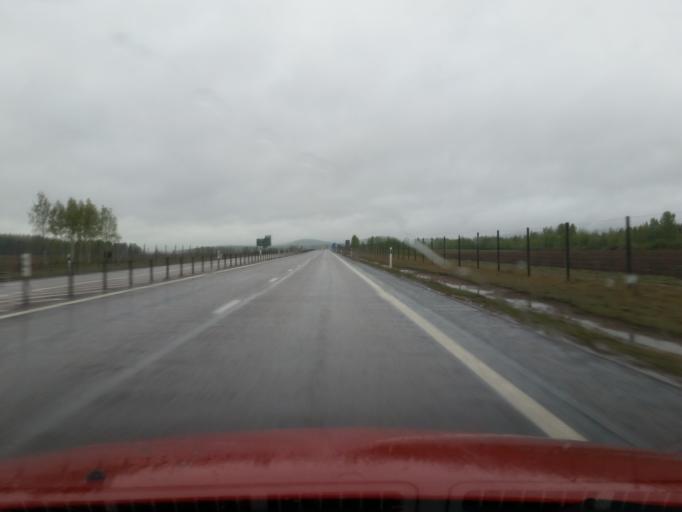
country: SE
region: Dalarna
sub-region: Borlange Kommun
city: Ornas
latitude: 60.4323
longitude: 15.5193
